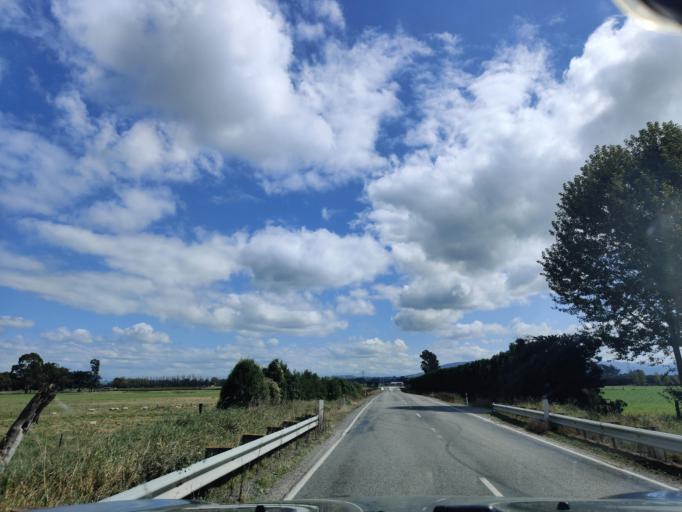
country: NZ
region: Canterbury
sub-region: Timaru District
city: Pleasant Point
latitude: -44.1262
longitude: 171.2557
